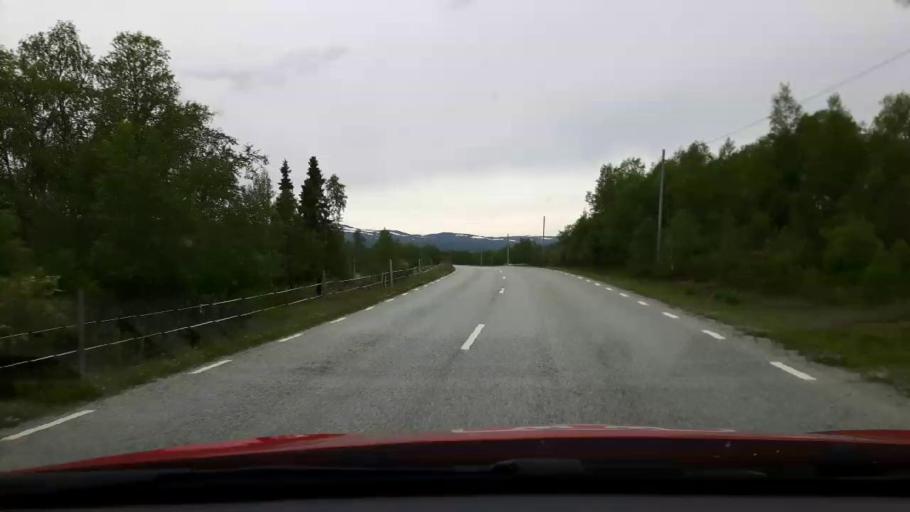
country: SE
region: Jaemtland
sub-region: Are Kommun
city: Are
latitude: 62.6022
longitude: 12.5181
